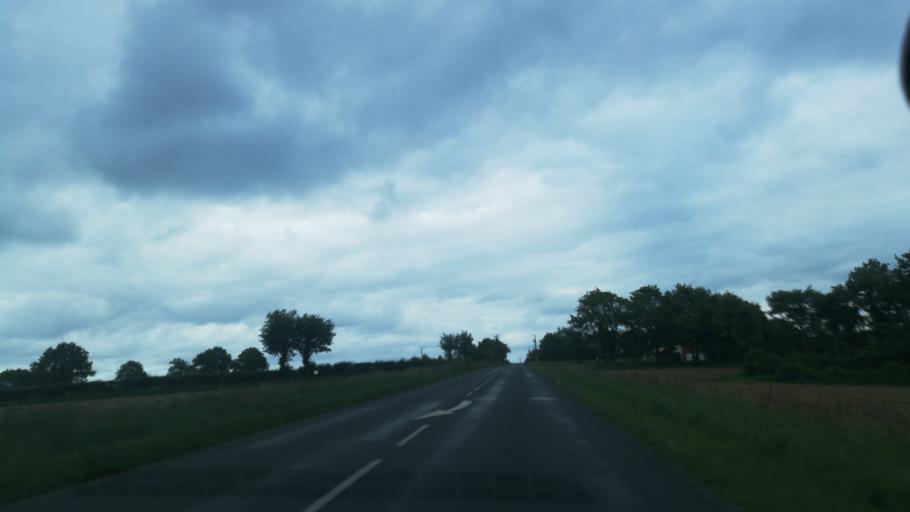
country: FR
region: Poitou-Charentes
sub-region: Departement des Deux-Sevres
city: Courlay
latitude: 46.7616
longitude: -0.5347
